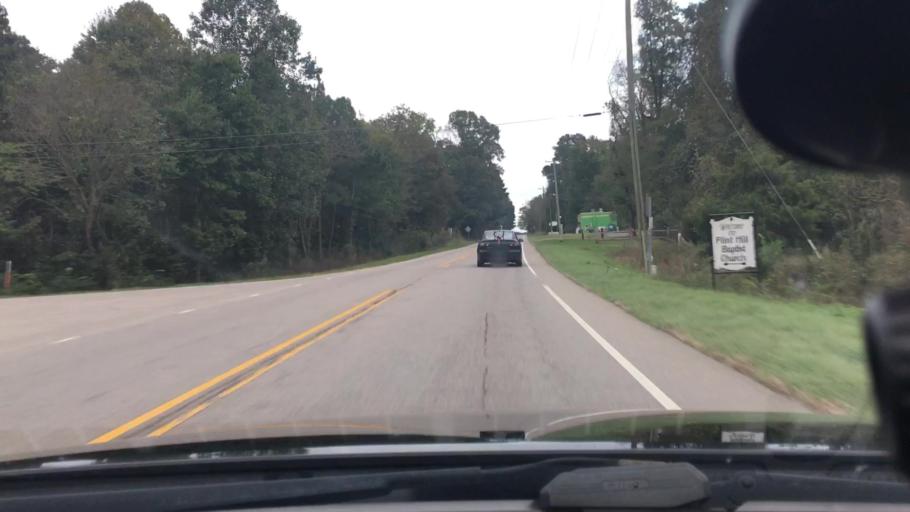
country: US
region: North Carolina
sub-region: Moore County
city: Robbins
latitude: 35.4029
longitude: -79.5594
